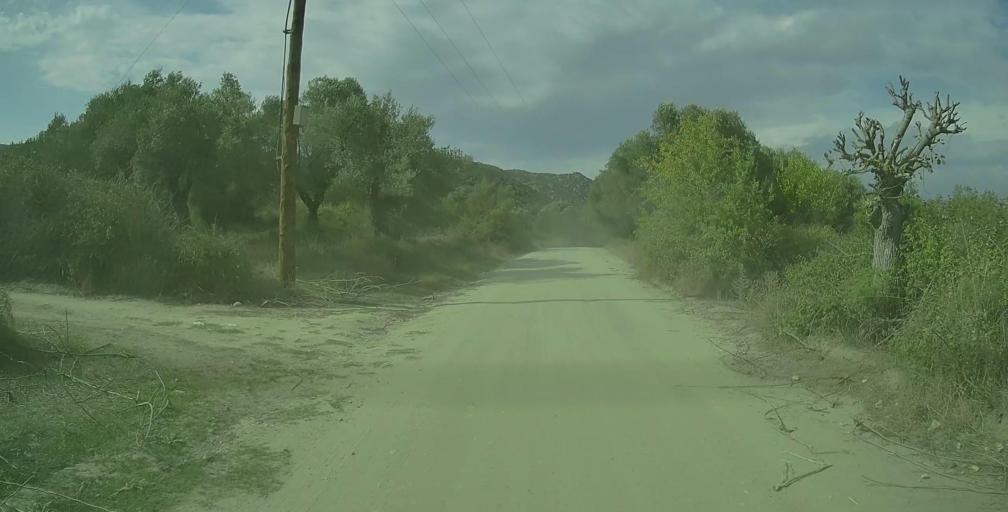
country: GR
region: Central Macedonia
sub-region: Nomos Chalkidikis
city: Sykia
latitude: 40.0275
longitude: 23.9452
